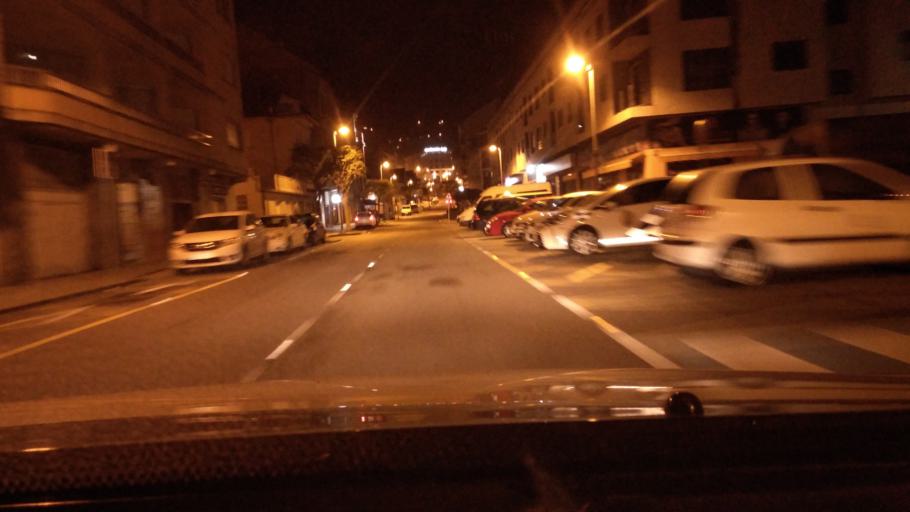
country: ES
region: Galicia
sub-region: Provincia de Pontevedra
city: Moana
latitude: 42.2868
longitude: -8.7335
